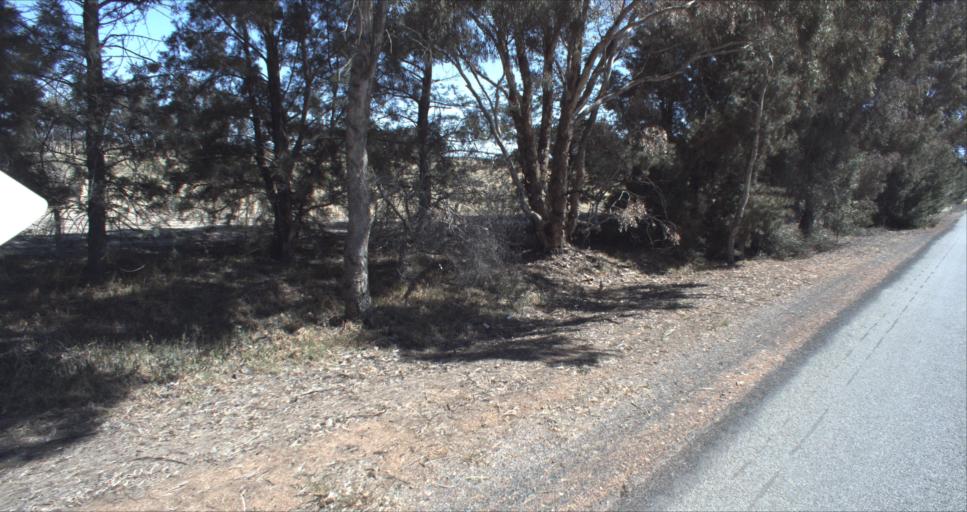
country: AU
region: New South Wales
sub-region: Leeton
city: Leeton
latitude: -34.5740
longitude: 146.3101
